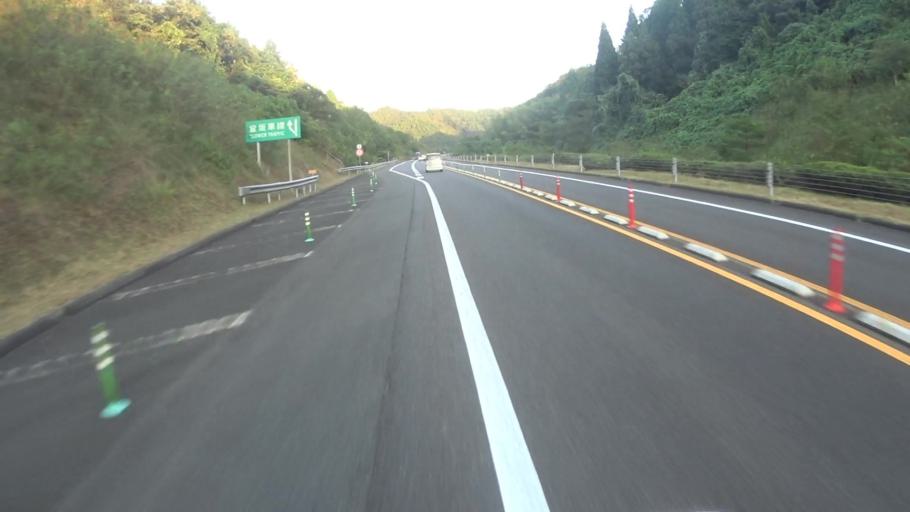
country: JP
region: Kyoto
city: Ayabe
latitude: 35.3835
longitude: 135.2466
